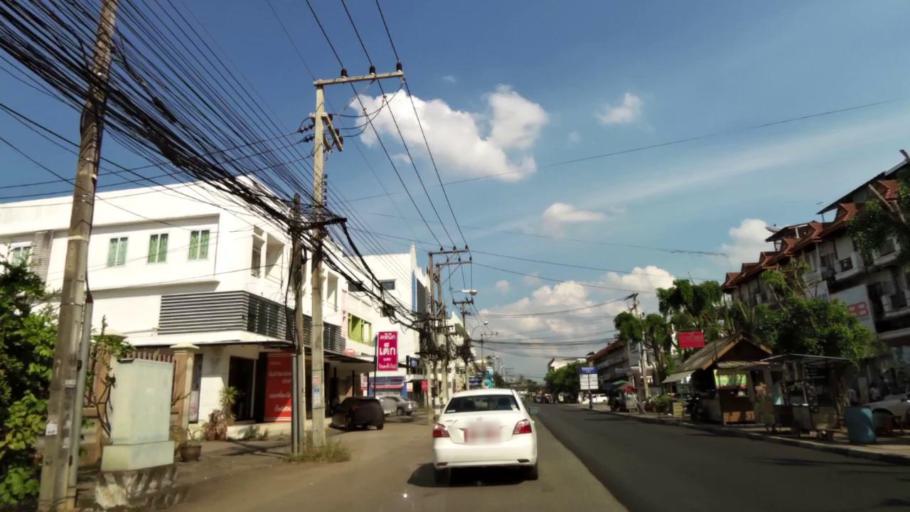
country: TH
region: Phrae
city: Phrae
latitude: 18.1364
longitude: 100.1435
